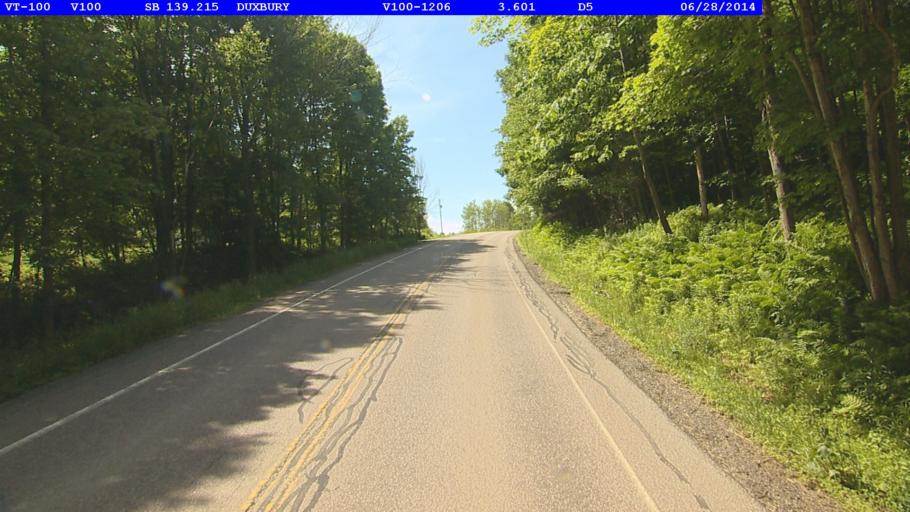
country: US
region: Vermont
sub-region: Washington County
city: Waterbury
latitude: 44.2962
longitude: -72.7745
